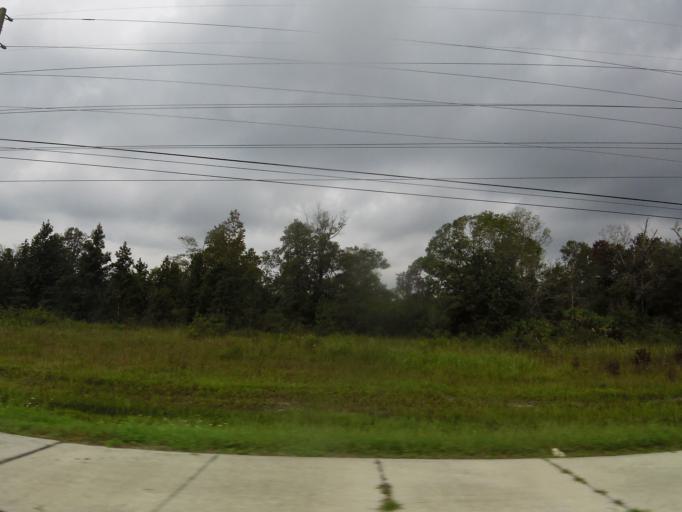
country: US
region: Florida
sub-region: Clay County
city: Middleburg
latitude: 30.1219
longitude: -81.8311
